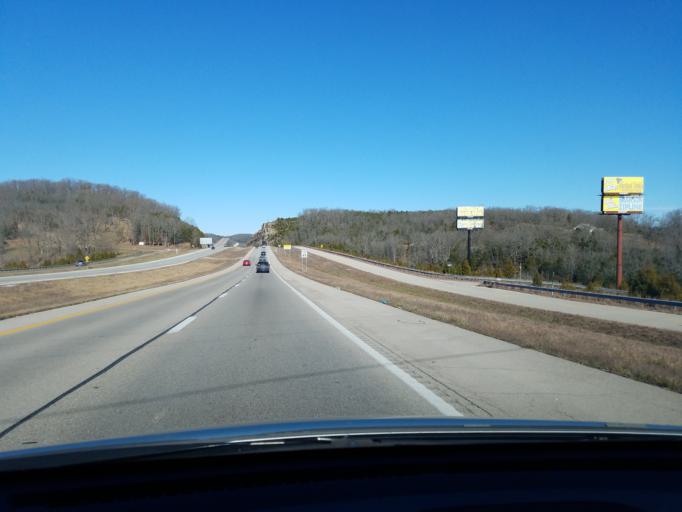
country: US
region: Missouri
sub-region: Taney County
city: Merriam Woods
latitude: 36.7567
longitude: -93.2225
